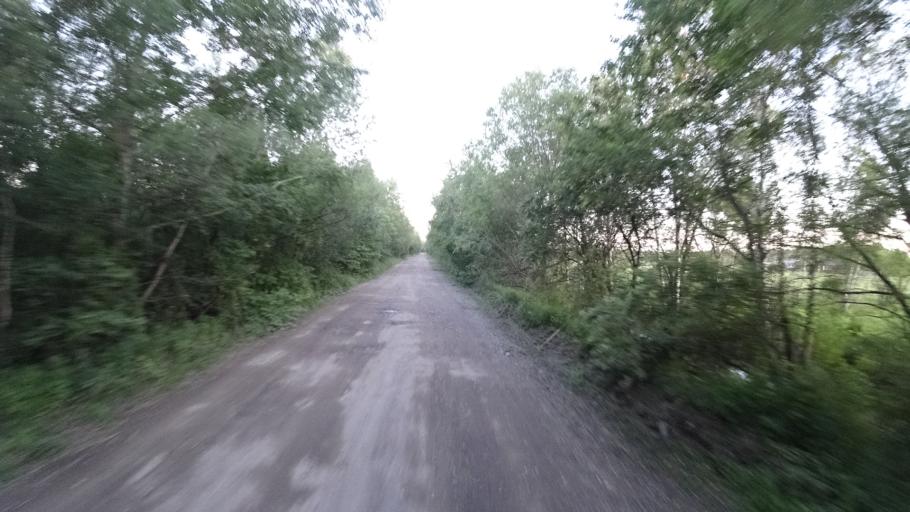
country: RU
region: Khabarovsk Krai
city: Khor
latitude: 47.8476
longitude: 134.9482
